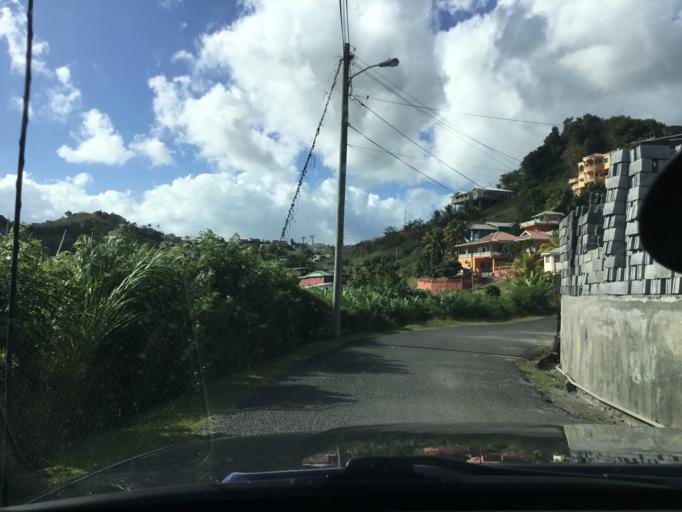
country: VC
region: Saint George
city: Kingstown
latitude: 13.1458
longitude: -61.1772
